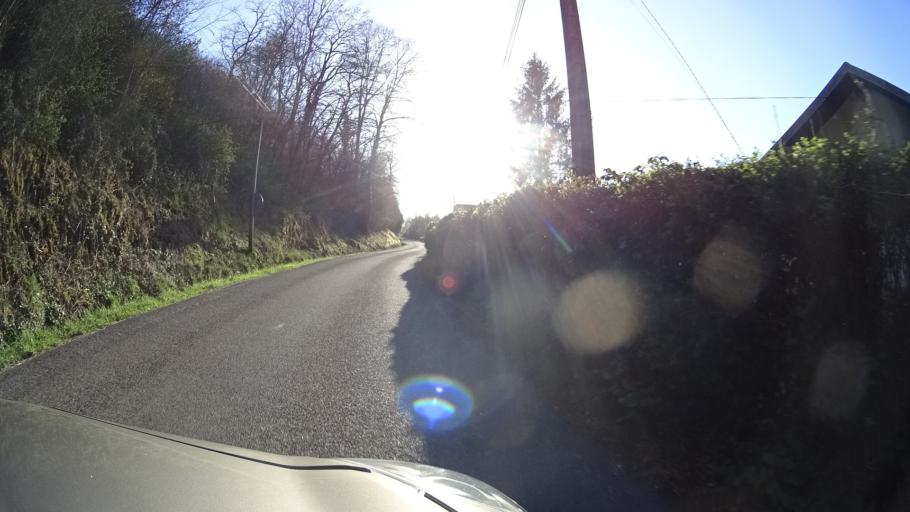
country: FR
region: Franche-Comte
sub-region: Departement du Doubs
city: Beure
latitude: 47.2006
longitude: 5.9974
